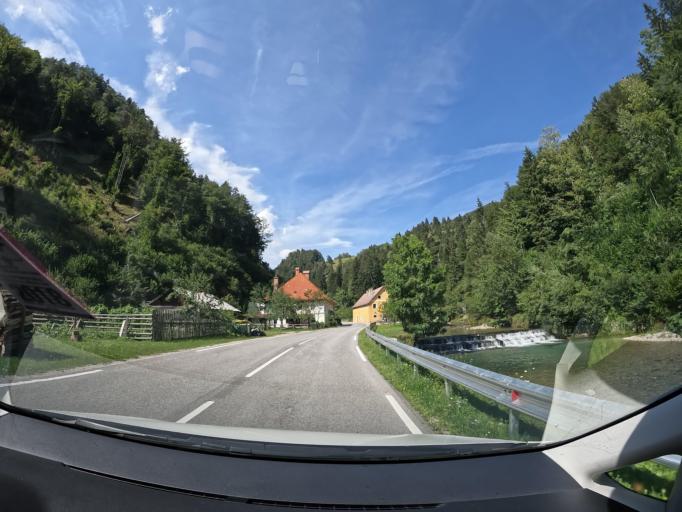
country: SI
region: Kranj
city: Golnik
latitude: 46.3805
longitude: 14.3899
